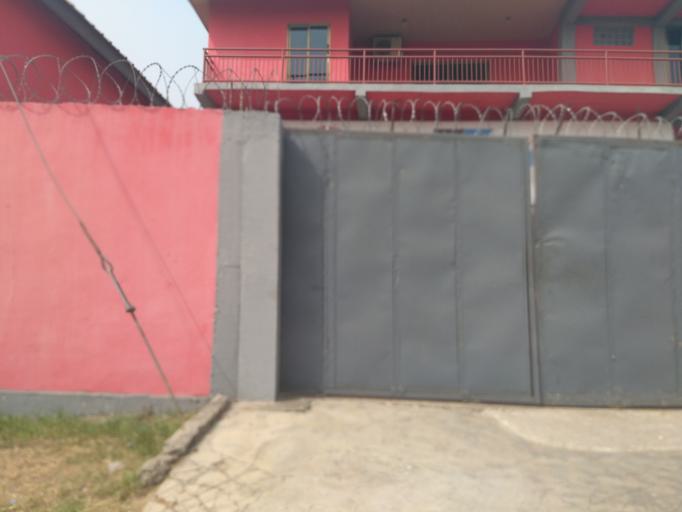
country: GH
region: Ashanti
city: Kumasi
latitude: 6.6778
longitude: -1.6058
